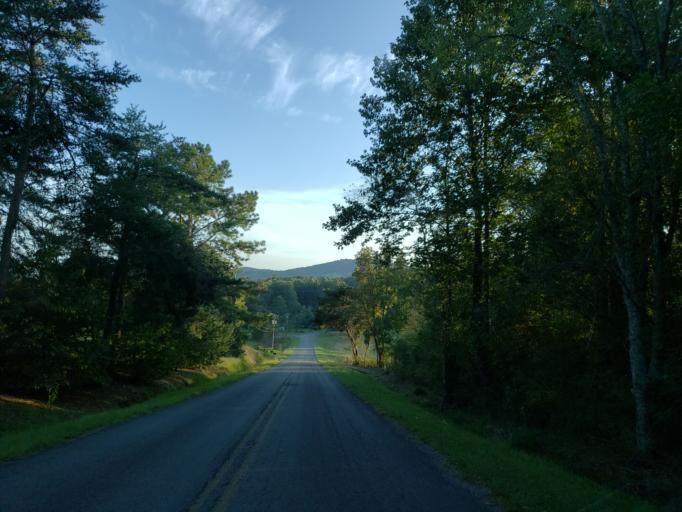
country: US
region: Georgia
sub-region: Gilmer County
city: Ellijay
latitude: 34.6560
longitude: -84.3382
